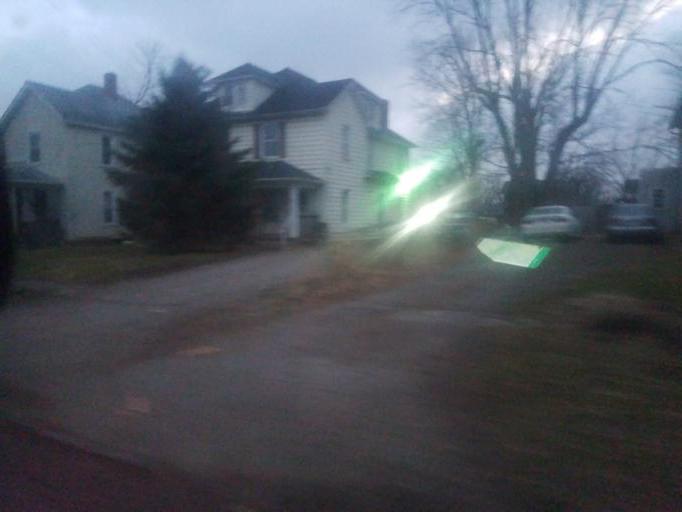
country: US
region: Ohio
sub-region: Marion County
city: Marion
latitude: 40.5836
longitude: -83.1351
